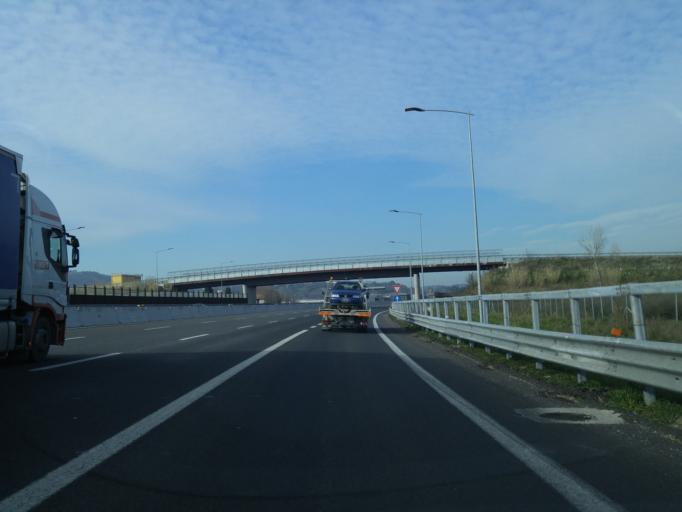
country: IT
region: The Marches
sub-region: Provincia di Pesaro e Urbino
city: Rosciano
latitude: 43.8158
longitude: 13.0107
